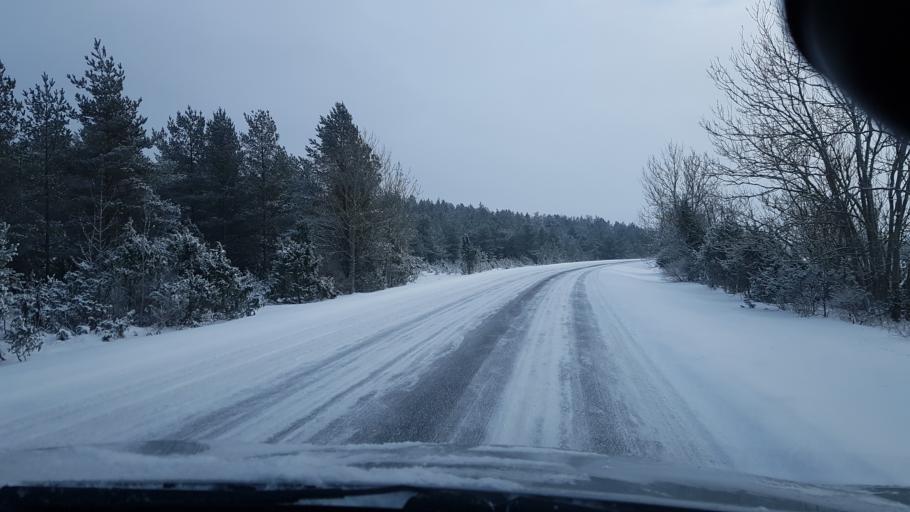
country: EE
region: Harju
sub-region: Keila linn
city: Keila
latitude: 59.3639
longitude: 24.4127
